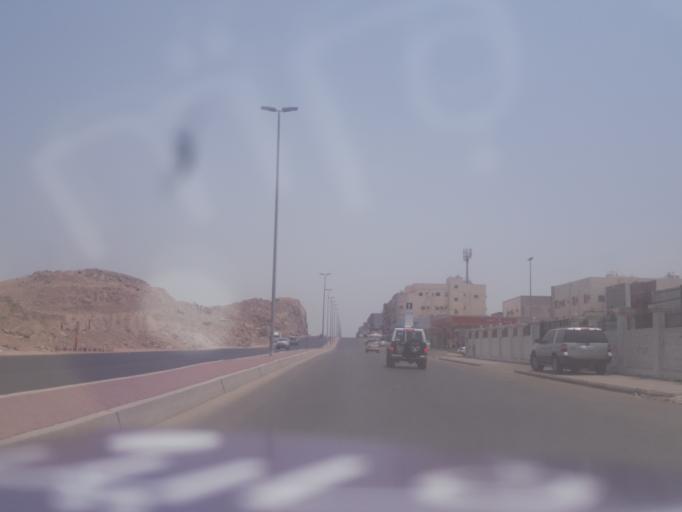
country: SA
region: Makkah
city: Jeddah
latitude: 21.4062
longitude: 39.2659
